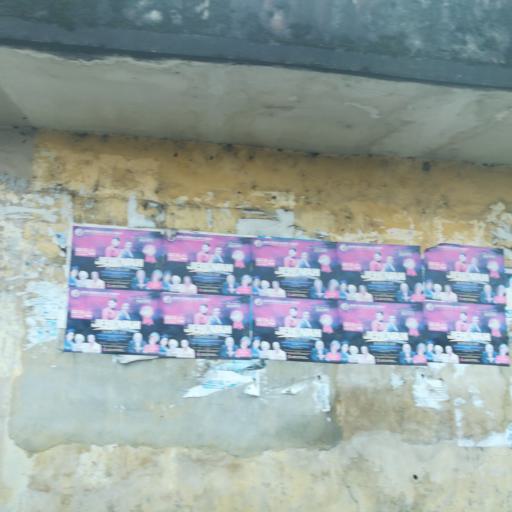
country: NG
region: Rivers
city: Port Harcourt
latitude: 4.8016
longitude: 7.0042
